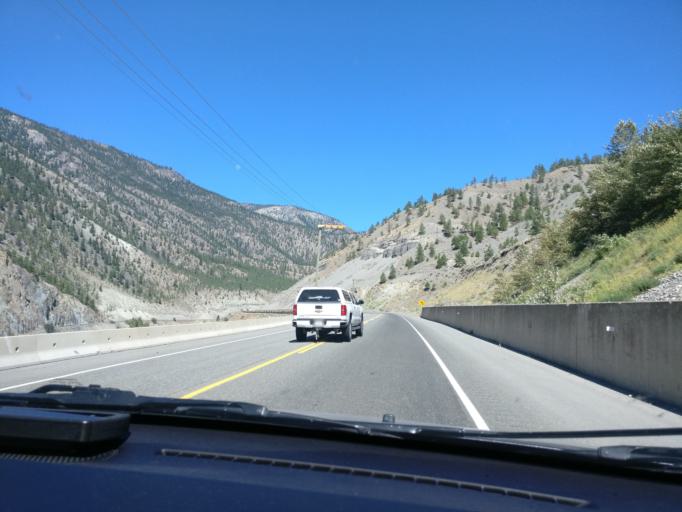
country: CA
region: British Columbia
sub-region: Thompson-Nicola Regional District
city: Ashcroft
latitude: 50.2720
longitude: -121.4016
